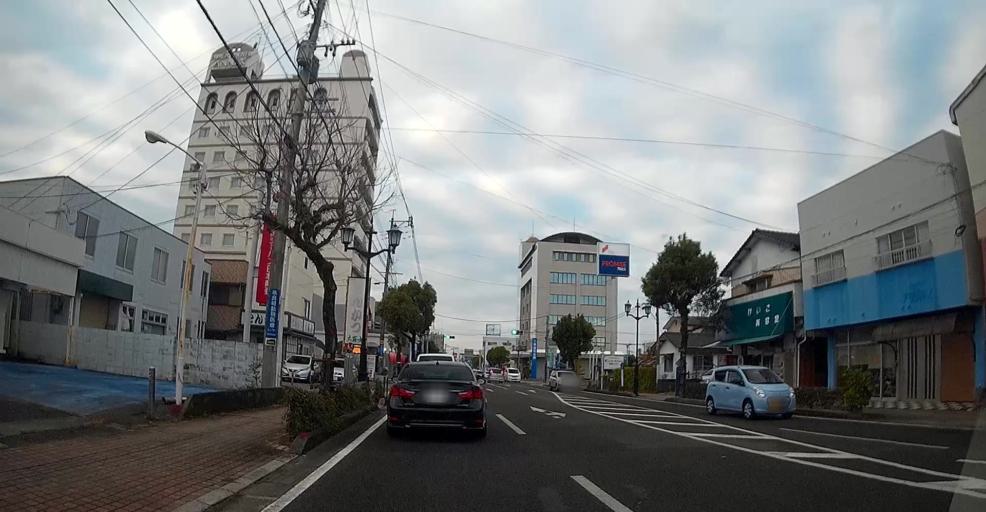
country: JP
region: Kumamoto
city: Hondo
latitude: 32.4505
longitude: 130.1981
